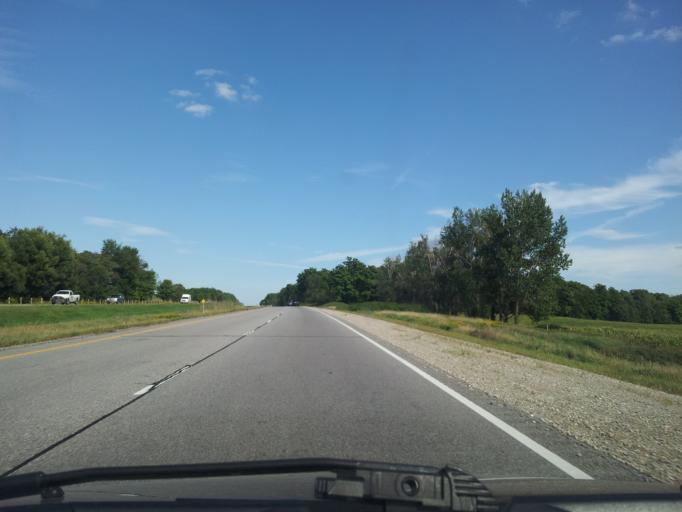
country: CA
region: Ontario
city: Kitchener
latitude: 43.3966
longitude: -80.6352
